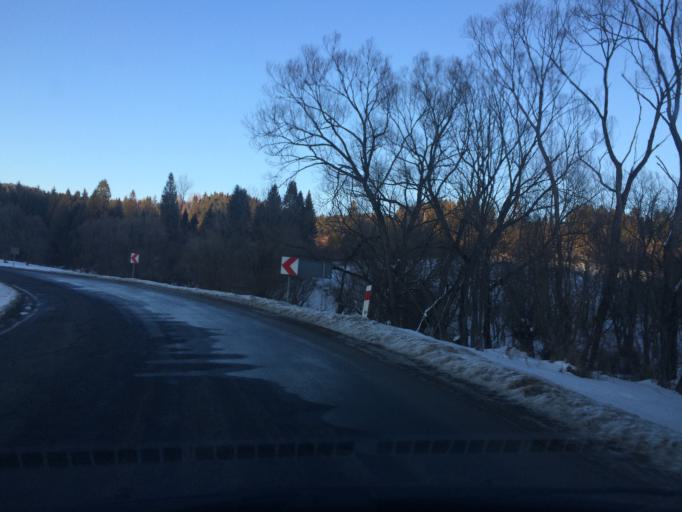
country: PL
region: Subcarpathian Voivodeship
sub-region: Powiat bieszczadzki
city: Lutowiska
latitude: 49.2294
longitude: 22.7018
